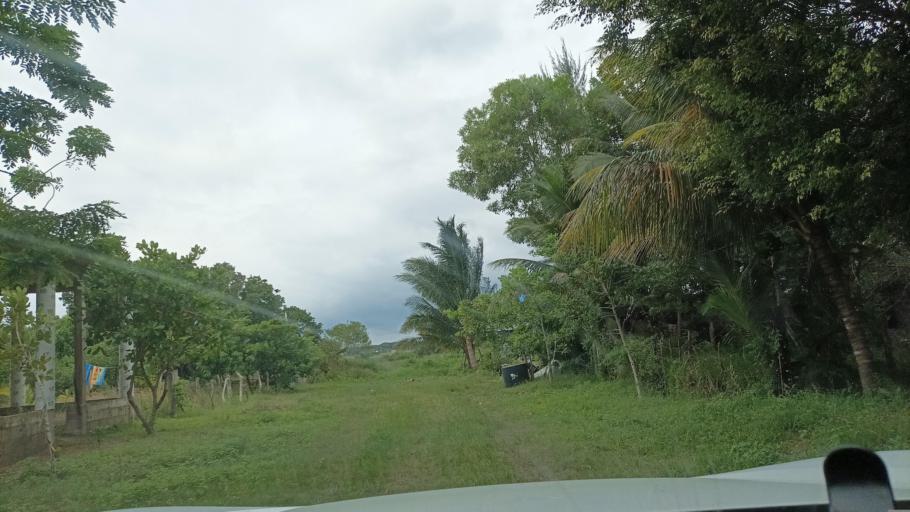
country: MX
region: Veracruz
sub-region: Coatzacoalcos
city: Fraccionamiento Ciudad Olmeca
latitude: 18.1810
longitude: -94.5928
